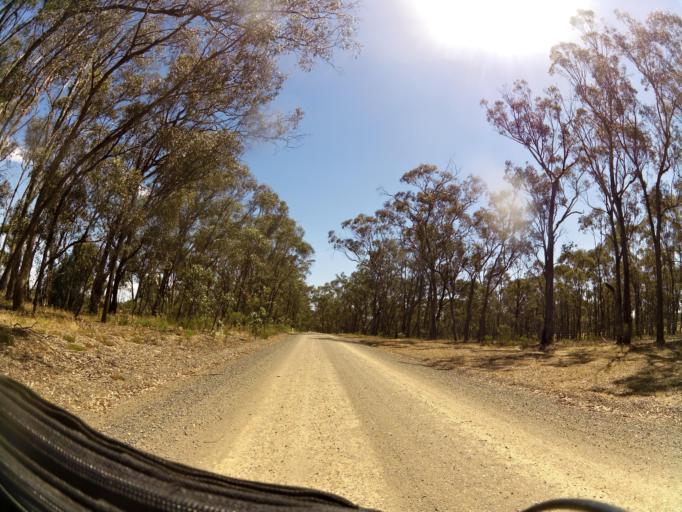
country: AU
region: Victoria
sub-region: Campaspe
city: Kyabram
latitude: -36.8404
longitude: 145.0715
